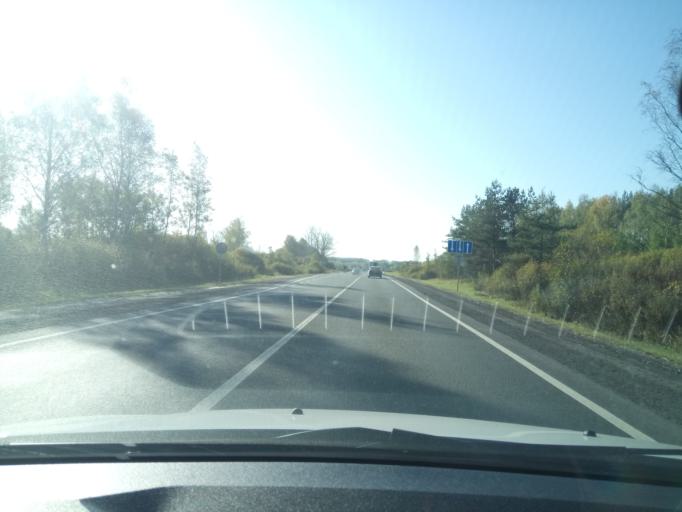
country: RU
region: Nizjnij Novgorod
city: Dal'neye Konstantinovo
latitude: 55.9670
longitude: 43.9742
